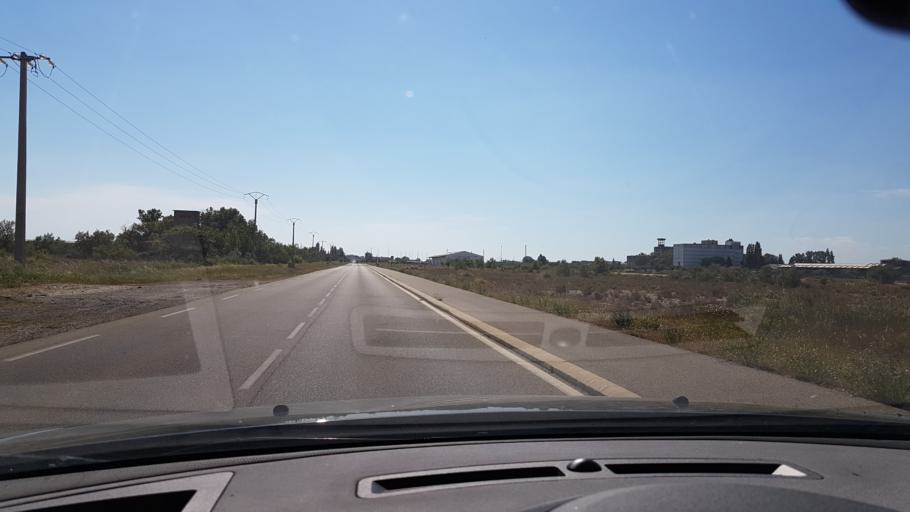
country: FR
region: Provence-Alpes-Cote d'Azur
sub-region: Departement des Bouches-du-Rhone
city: Port-Saint-Louis-du-Rhone
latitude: 43.3851
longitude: 4.8294
